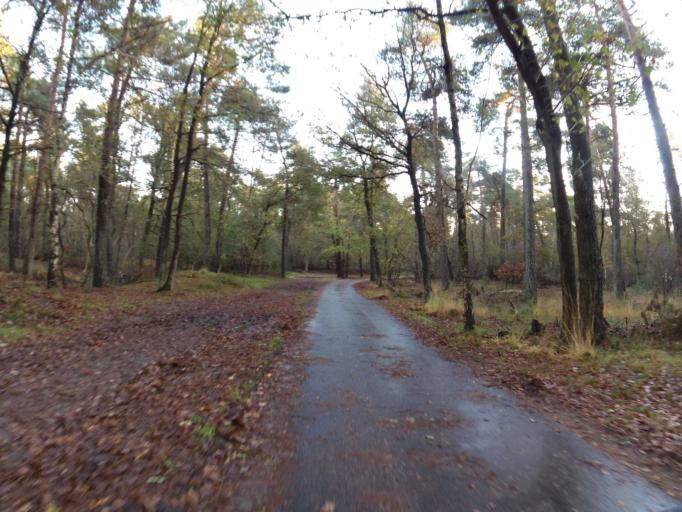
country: NL
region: North Brabant
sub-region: Gemeente Loon op Zand
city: Loon op Zand
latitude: 51.6469
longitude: 5.0838
